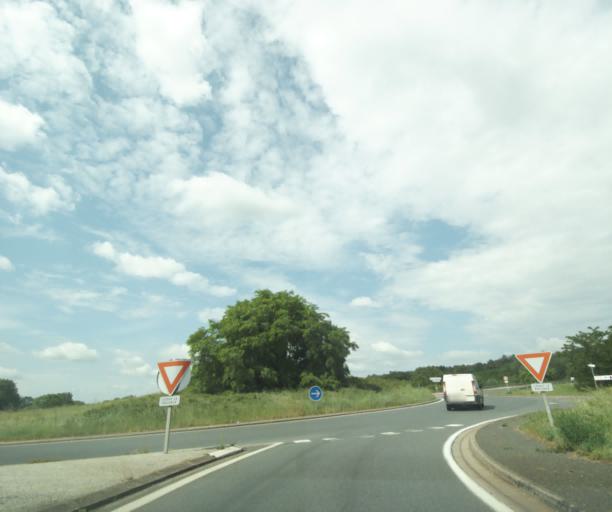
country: FR
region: Pays de la Loire
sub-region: Departement de Maine-et-Loire
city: Distre
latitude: 47.2349
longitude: -0.1119
